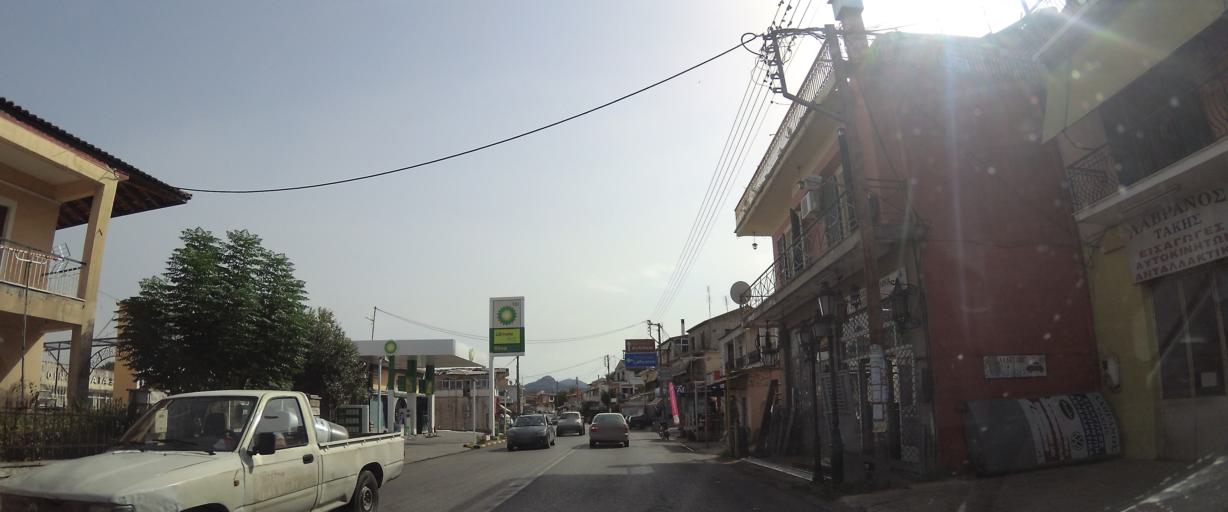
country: GR
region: Ionian Islands
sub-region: Nomos Kerkyras
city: Viros
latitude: 39.5914
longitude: 19.8928
